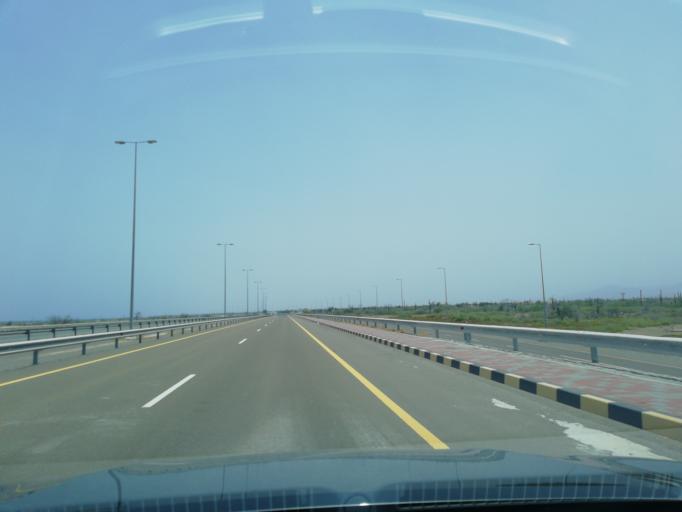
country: OM
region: Al Batinah
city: Shinas
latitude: 24.8798
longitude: 56.4043
